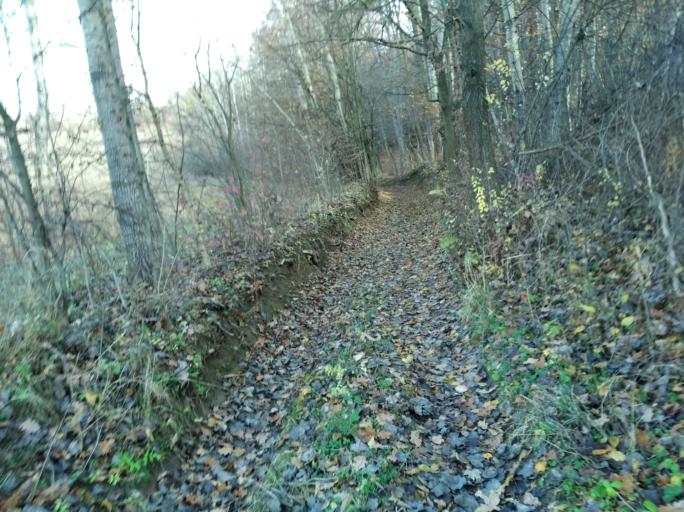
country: PL
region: Subcarpathian Voivodeship
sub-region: Powiat strzyzowski
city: Strzyzow
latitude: 49.8432
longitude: 21.8328
